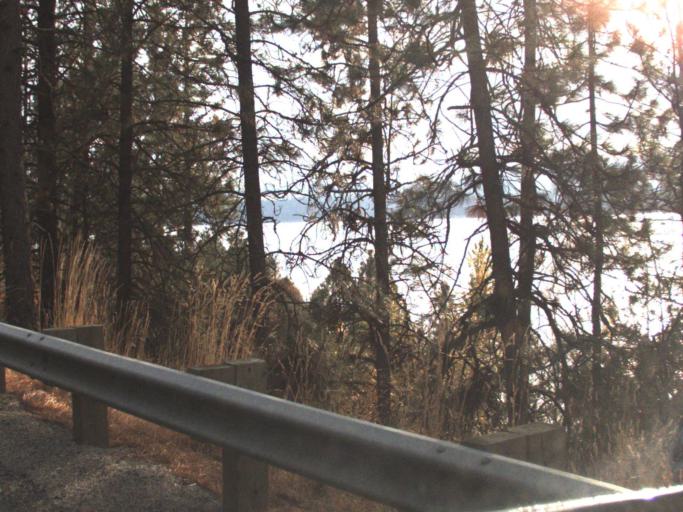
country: US
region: Washington
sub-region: Stevens County
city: Kettle Falls
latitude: 48.3222
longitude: -118.1511
